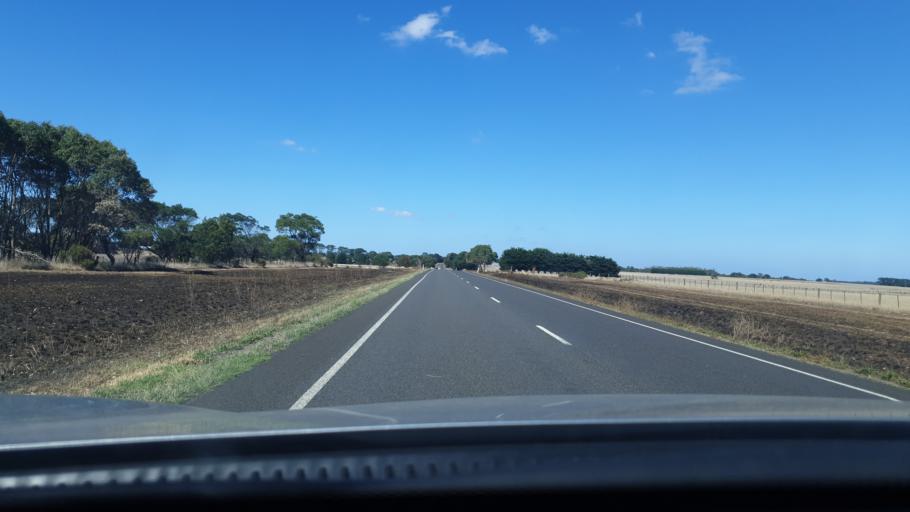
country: AU
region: Victoria
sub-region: Warrnambool
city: Warrnambool
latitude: -38.1737
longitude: 142.4107
